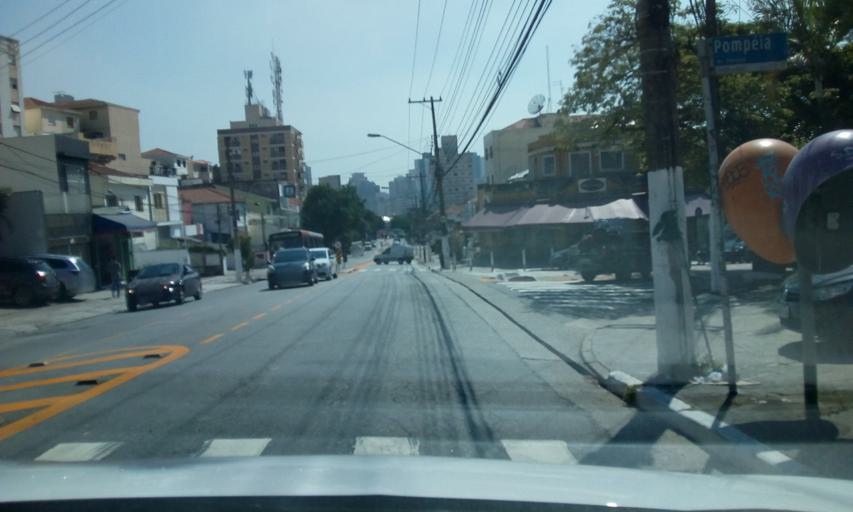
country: BR
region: Sao Paulo
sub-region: Sao Paulo
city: Sao Paulo
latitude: -23.5421
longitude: -46.6903
